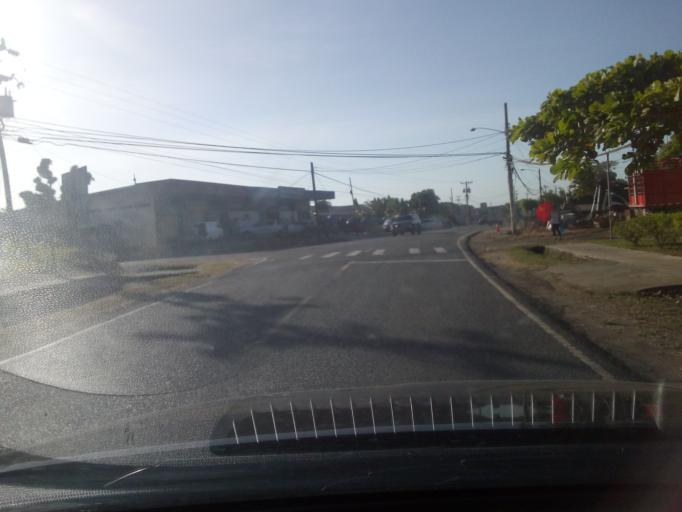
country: PA
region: Veraguas
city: Atalaya
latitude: 8.0467
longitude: -80.9310
